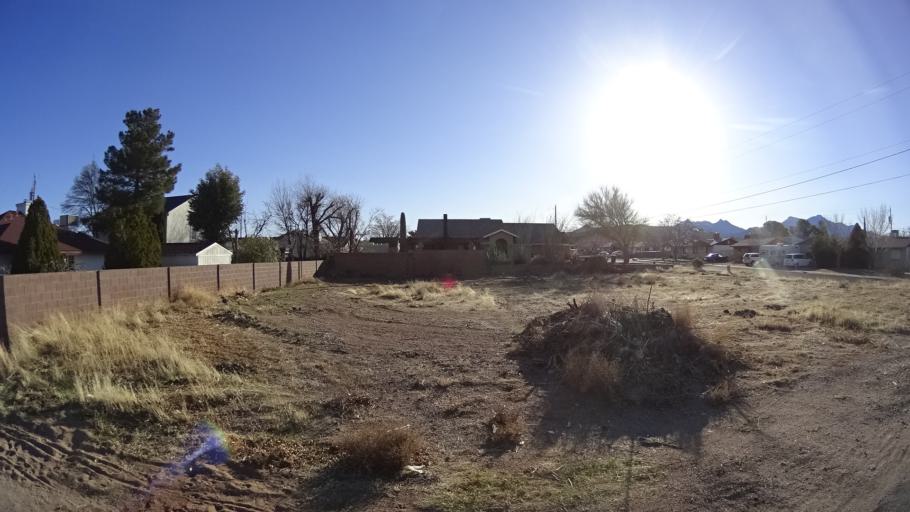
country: US
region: Arizona
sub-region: Mohave County
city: Kingman
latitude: 35.1960
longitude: -114.0181
